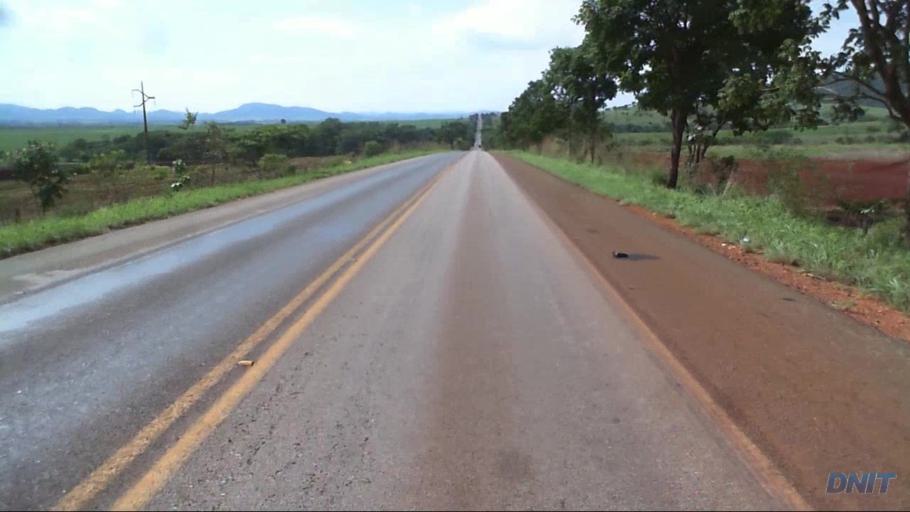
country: BR
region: Goias
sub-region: Barro Alto
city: Barro Alto
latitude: -15.0028
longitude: -48.9040
